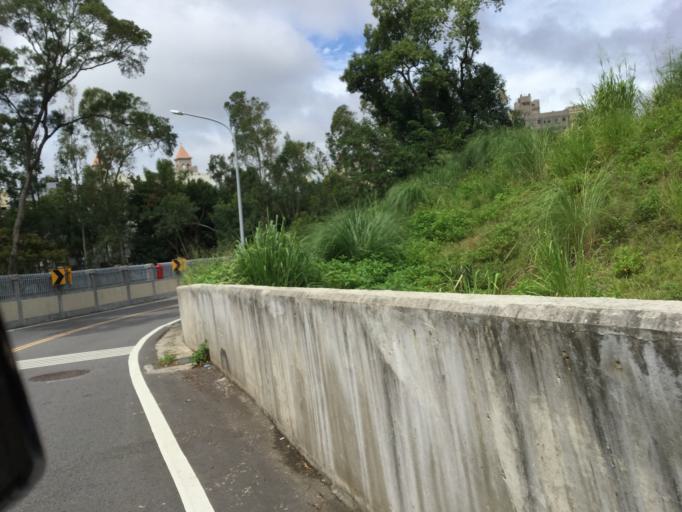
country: TW
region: Taiwan
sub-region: Hsinchu
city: Hsinchu
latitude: 24.7807
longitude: 121.0138
